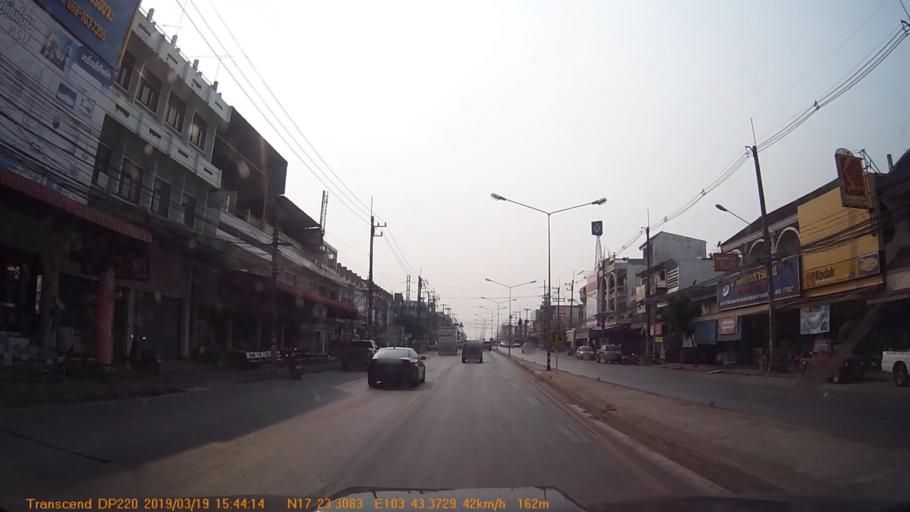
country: TH
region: Sakon Nakhon
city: Phang Khon
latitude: 17.3885
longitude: 103.7228
